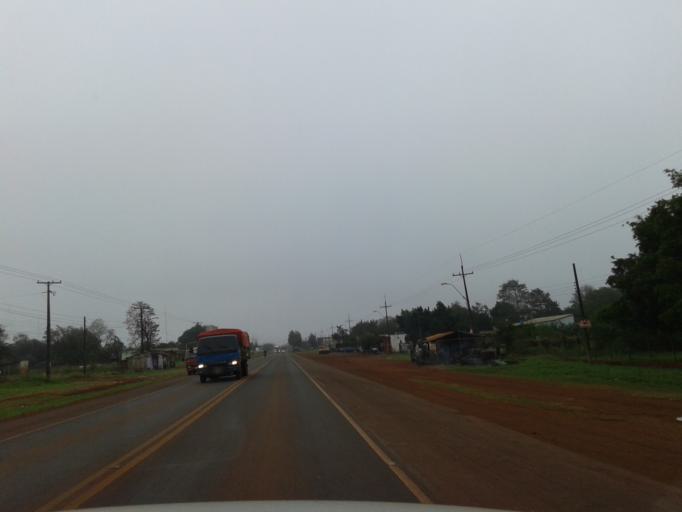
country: PY
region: Alto Parana
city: Colonia Yguazu
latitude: -25.4992
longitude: -54.8985
